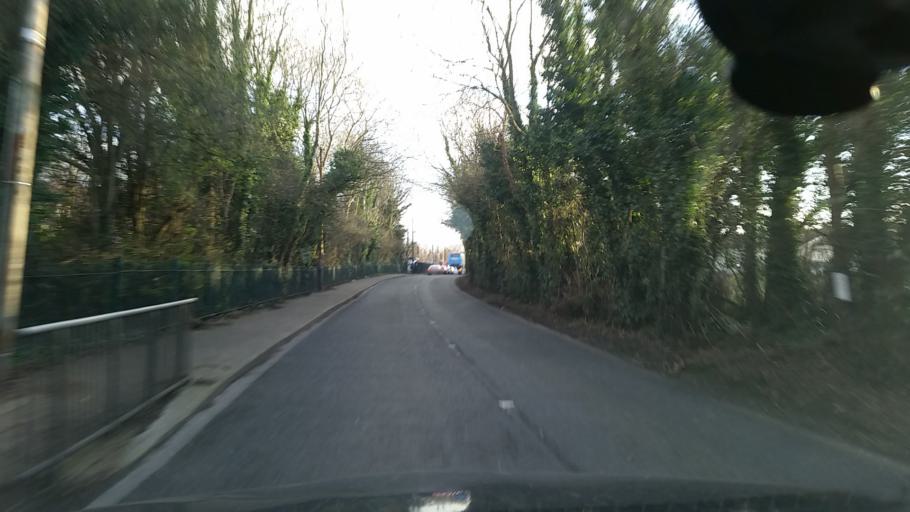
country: IE
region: Leinster
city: Hartstown
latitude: 53.3888
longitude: -6.4091
